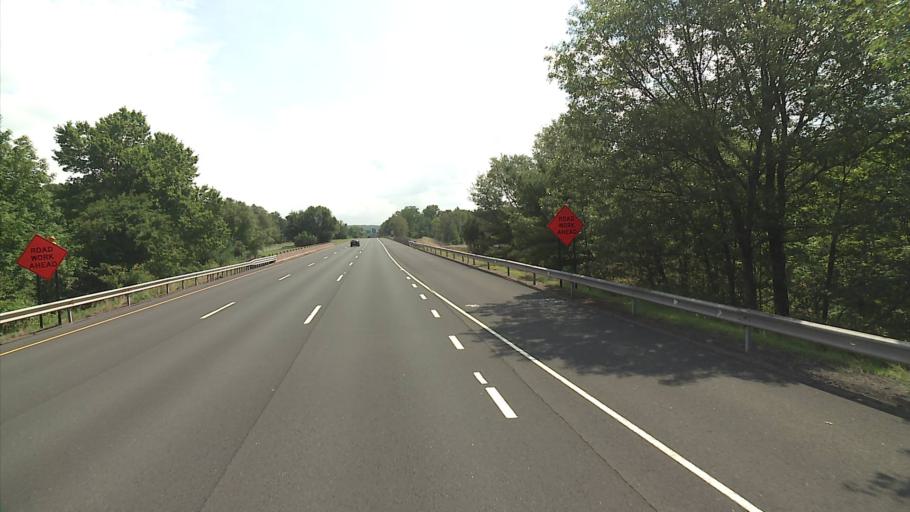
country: US
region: Connecticut
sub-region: Hartford County
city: Manchester
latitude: 41.7676
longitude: -72.4818
